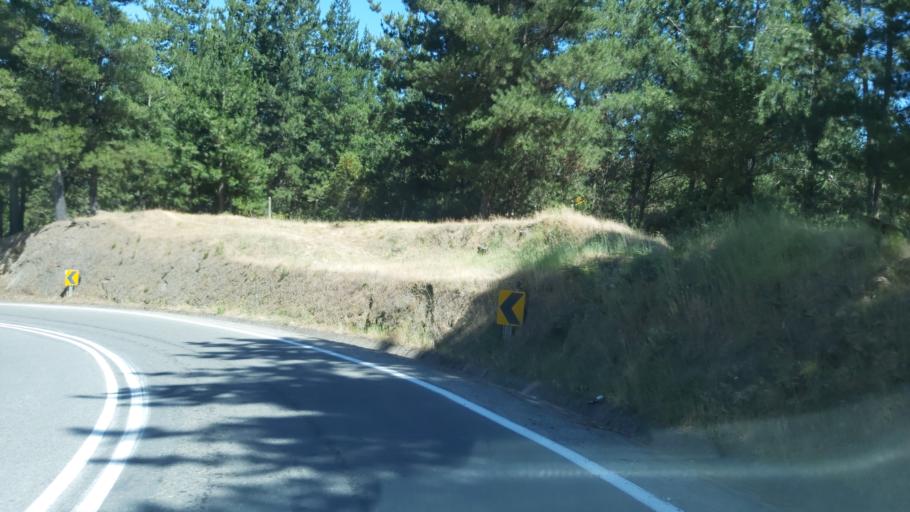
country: CL
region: Maule
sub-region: Provincia de Talca
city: Talca
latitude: -34.9794
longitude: -71.9714
